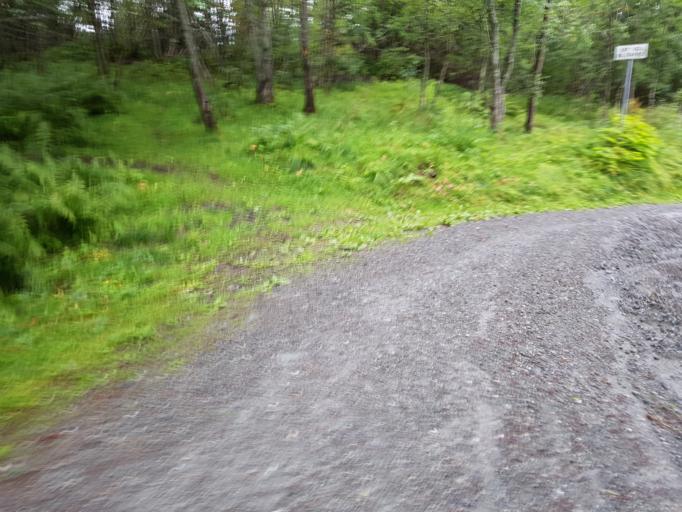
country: NO
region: Sor-Trondelag
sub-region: Trondheim
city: Trondheim
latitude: 63.3992
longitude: 10.4657
